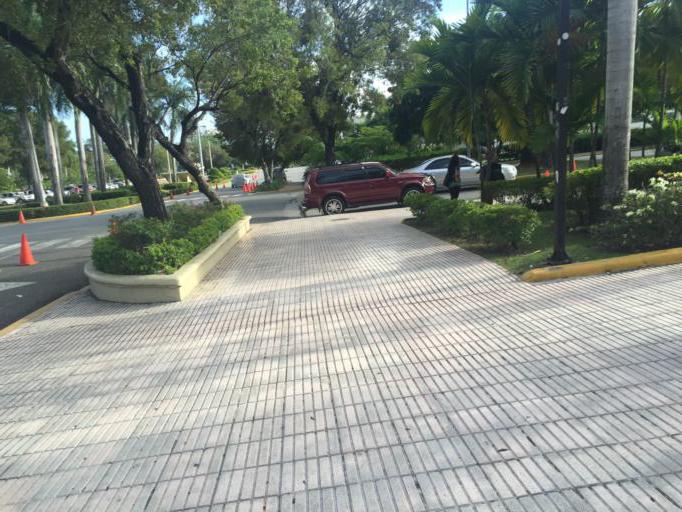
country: DO
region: Nacional
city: La Julia
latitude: 18.4616
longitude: -69.9193
